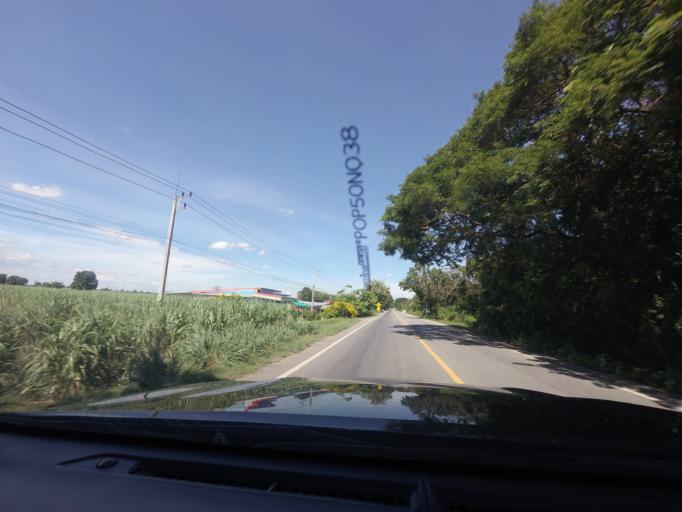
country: TH
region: Suphan Buri
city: Song Phi Nong
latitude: 14.1640
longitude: 99.9089
